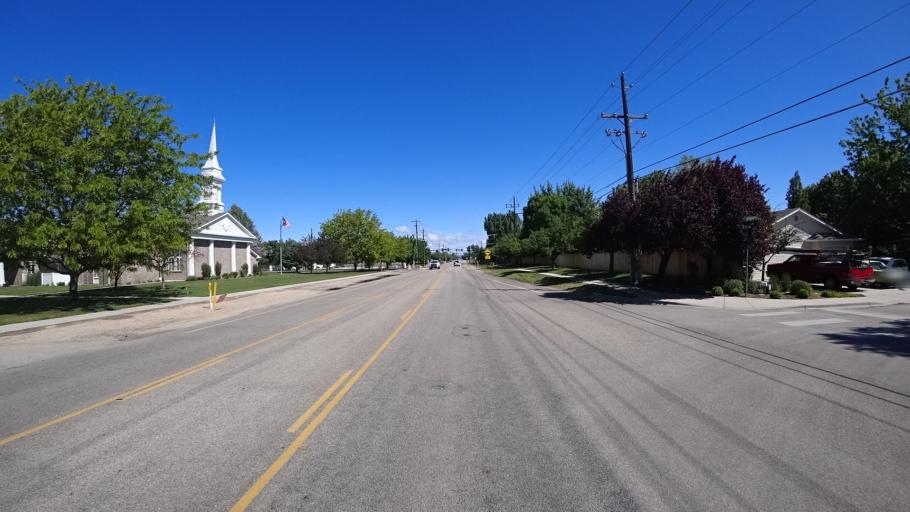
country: US
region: Idaho
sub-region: Ada County
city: Meridian
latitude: 43.6359
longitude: -116.3745
